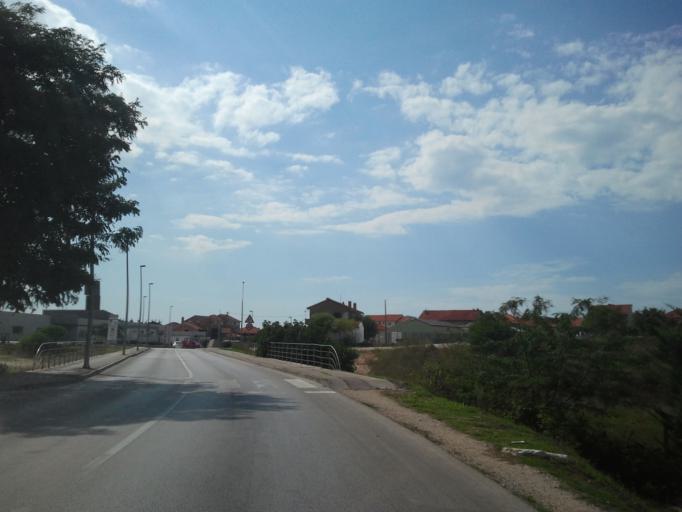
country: HR
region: Zadarska
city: Zadar
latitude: 44.1053
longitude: 15.2568
